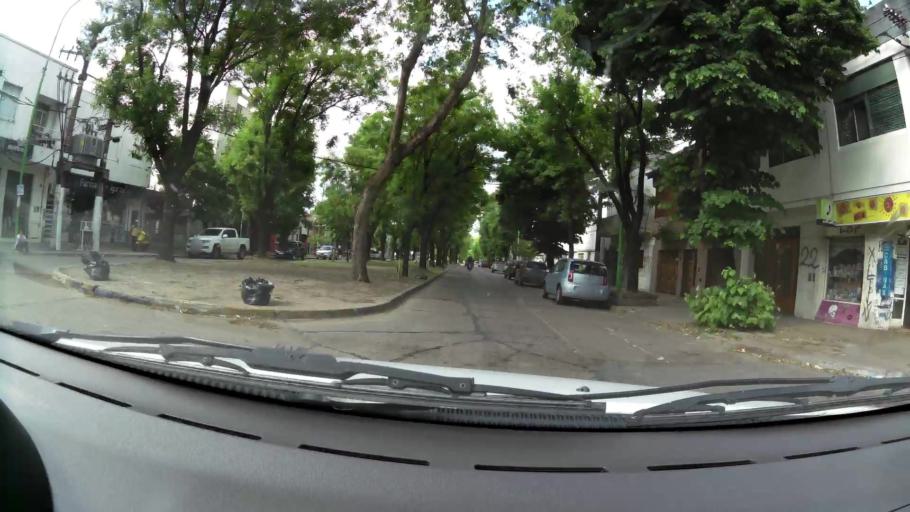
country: AR
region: Buenos Aires
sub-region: Partido de La Plata
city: La Plata
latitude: -34.9175
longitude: -57.9254
